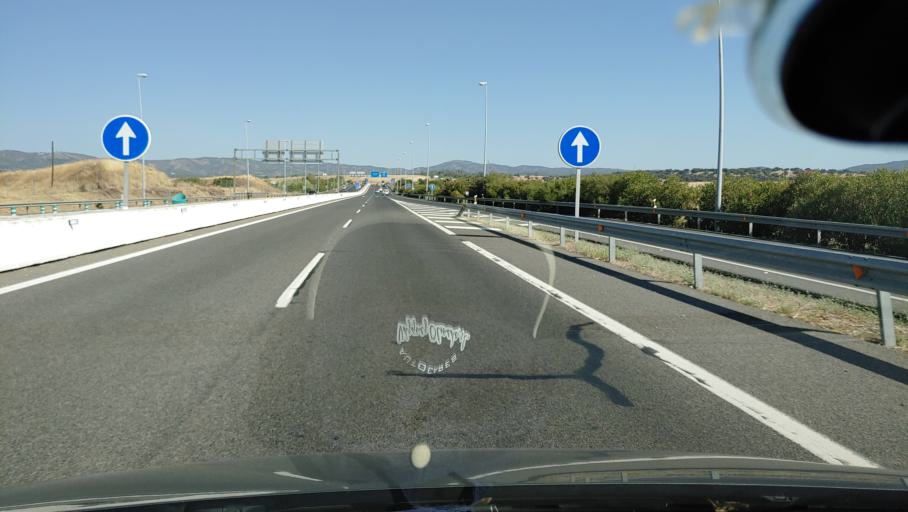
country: ES
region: Andalusia
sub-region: Province of Cordoba
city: Cordoba
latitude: 37.8980
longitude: -4.7479
